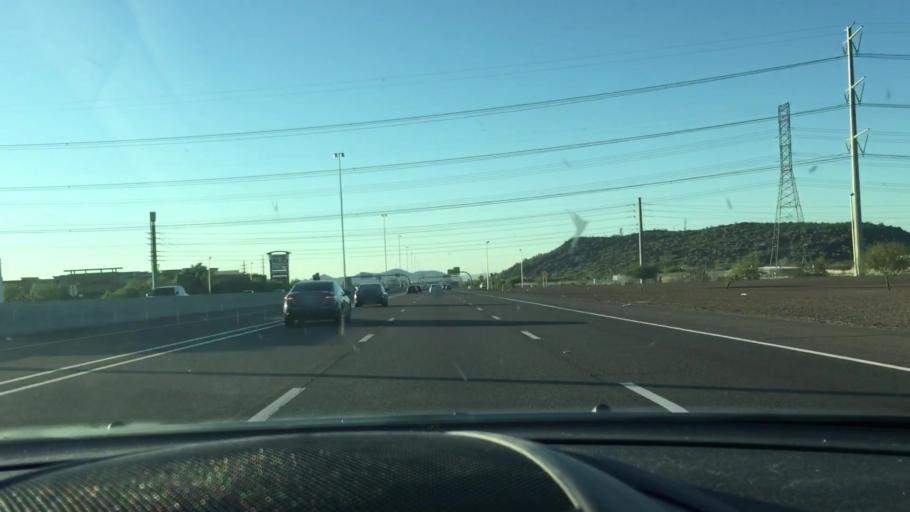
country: US
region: Arizona
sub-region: Maricopa County
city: Anthem
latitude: 33.7113
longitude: -112.1174
